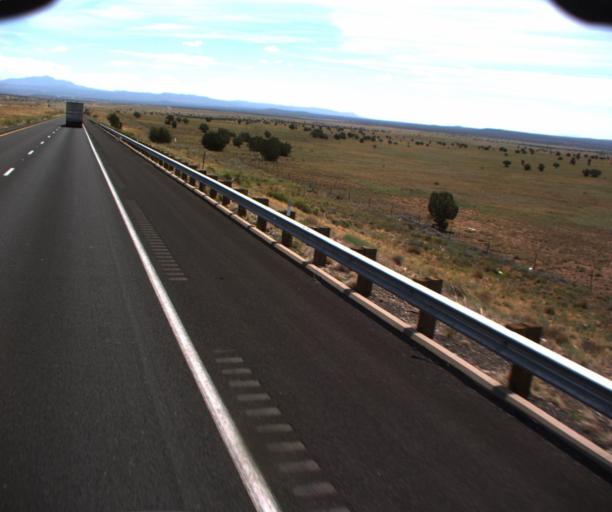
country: US
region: Arizona
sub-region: Yavapai County
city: Paulden
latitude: 35.2341
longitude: -112.6259
